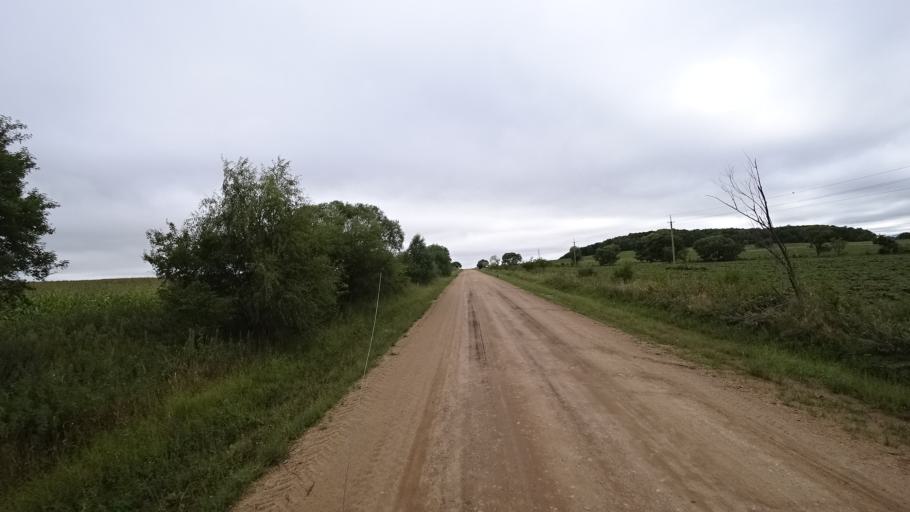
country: RU
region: Primorskiy
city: Monastyrishche
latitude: 44.0946
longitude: 132.6004
